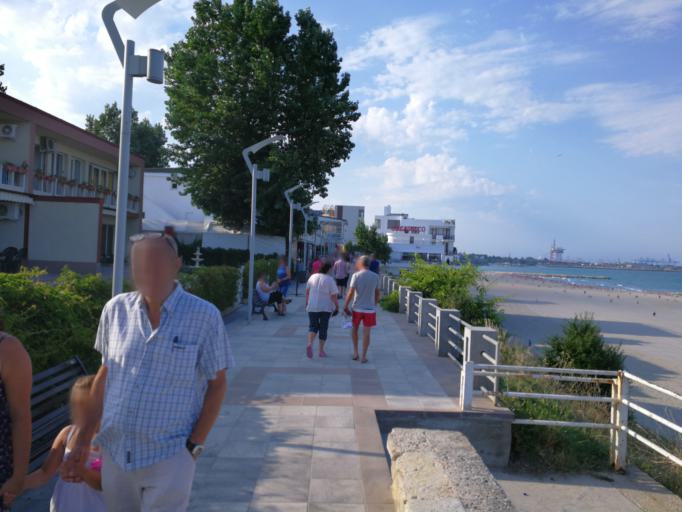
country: RO
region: Constanta
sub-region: Oras Eforie
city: Eforie Nord
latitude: 44.0695
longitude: 28.6385
